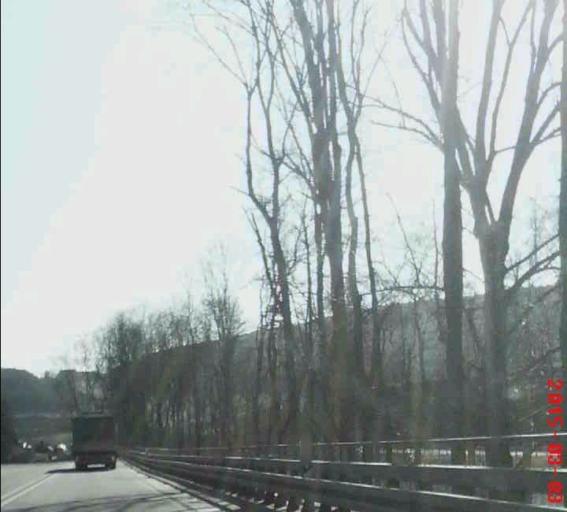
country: DE
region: Thuringia
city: Bad Blankenburg
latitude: 50.7245
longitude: 11.2631
